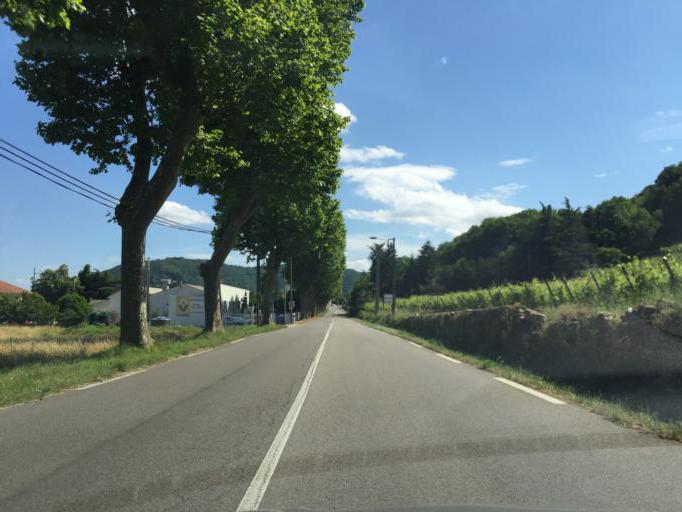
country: FR
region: Rhone-Alpes
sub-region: Departement de l'Ardeche
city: Saint-Jean-de-Muzols
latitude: 45.0902
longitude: 4.8180
